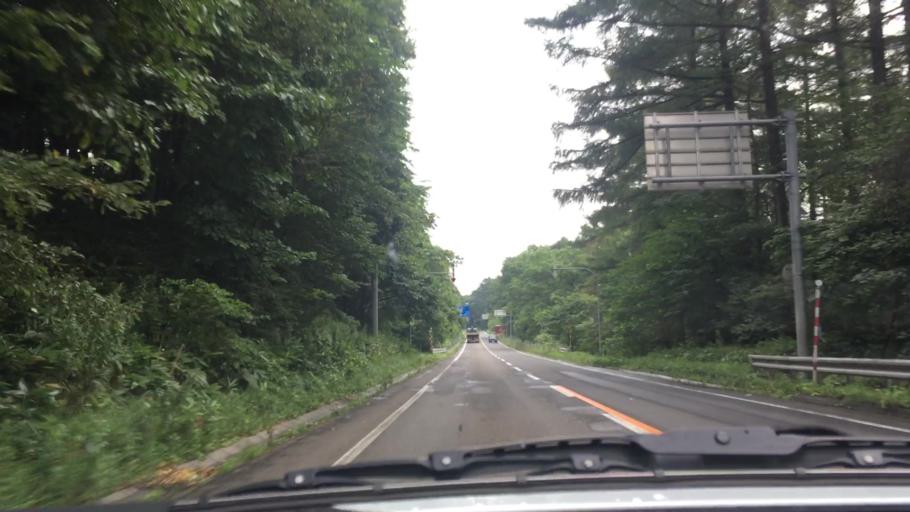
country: JP
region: Hokkaido
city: Chitose
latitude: 42.9448
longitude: 141.7418
